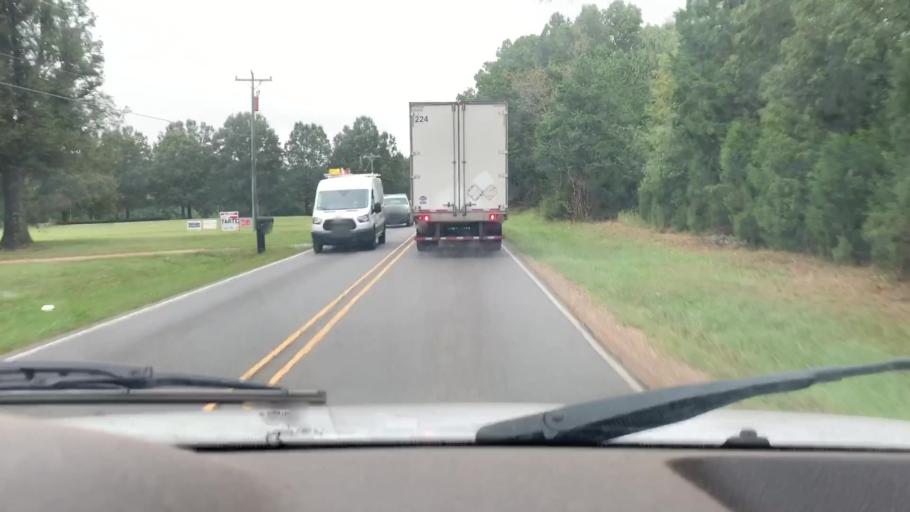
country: US
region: North Carolina
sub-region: Mecklenburg County
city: Huntersville
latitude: 35.3548
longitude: -80.8225
